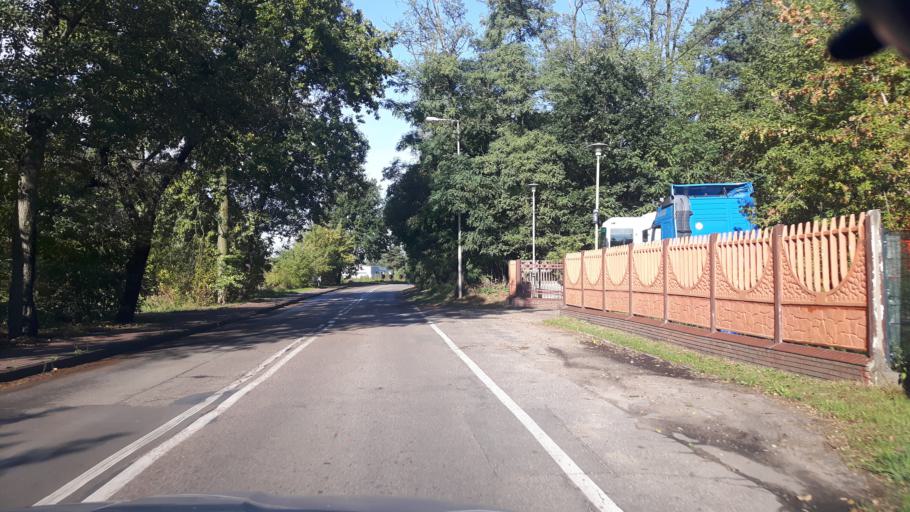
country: PL
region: Masovian Voivodeship
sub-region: Powiat legionowski
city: Nieporet
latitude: 52.3921
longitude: 21.0089
